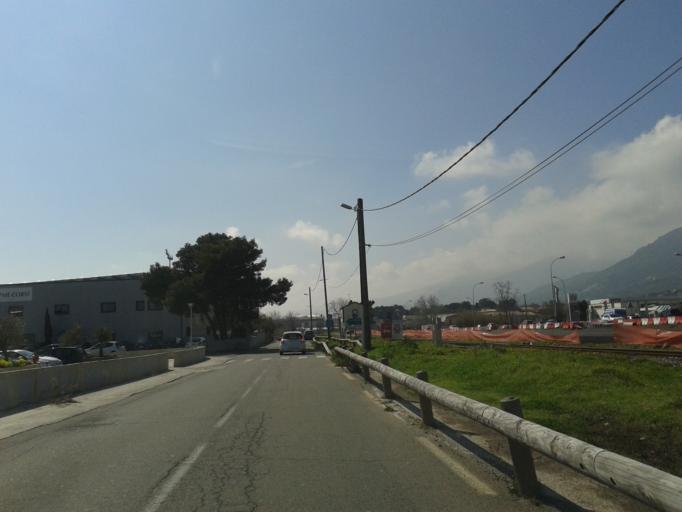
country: FR
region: Corsica
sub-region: Departement de la Haute-Corse
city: Furiani
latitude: 42.6534
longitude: 9.4416
